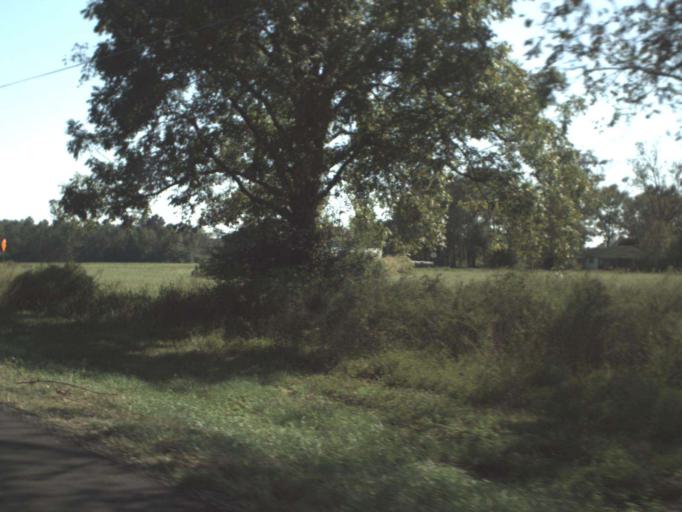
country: US
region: Florida
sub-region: Walton County
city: DeFuniak Springs
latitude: 30.8105
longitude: -86.2014
